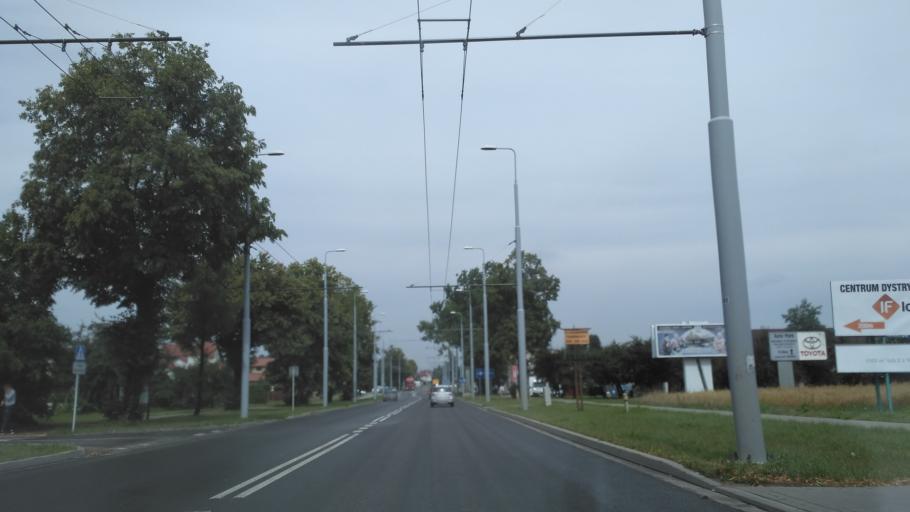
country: PL
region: Lublin Voivodeship
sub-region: Powiat lubelski
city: Lublin
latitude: 51.1987
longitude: 22.5860
